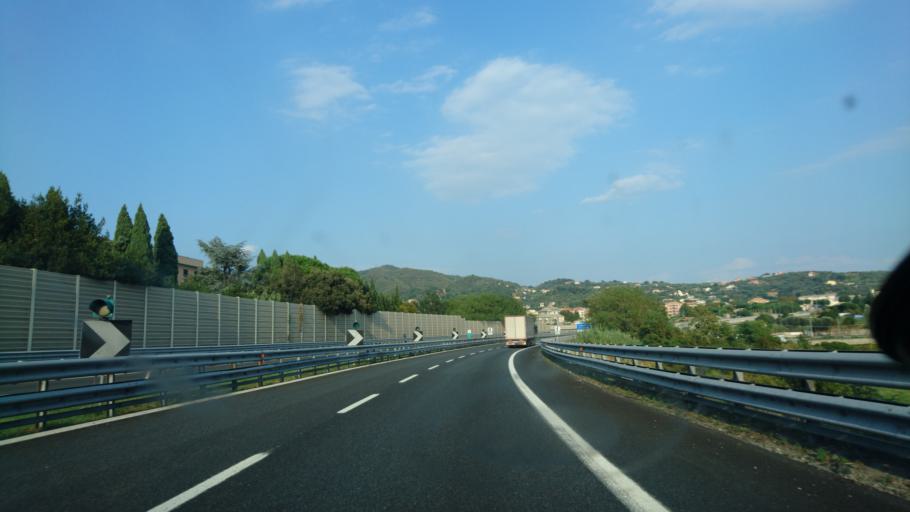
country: IT
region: Liguria
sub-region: Provincia di Savona
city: Albisola Marina
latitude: 44.3341
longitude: 8.5016
